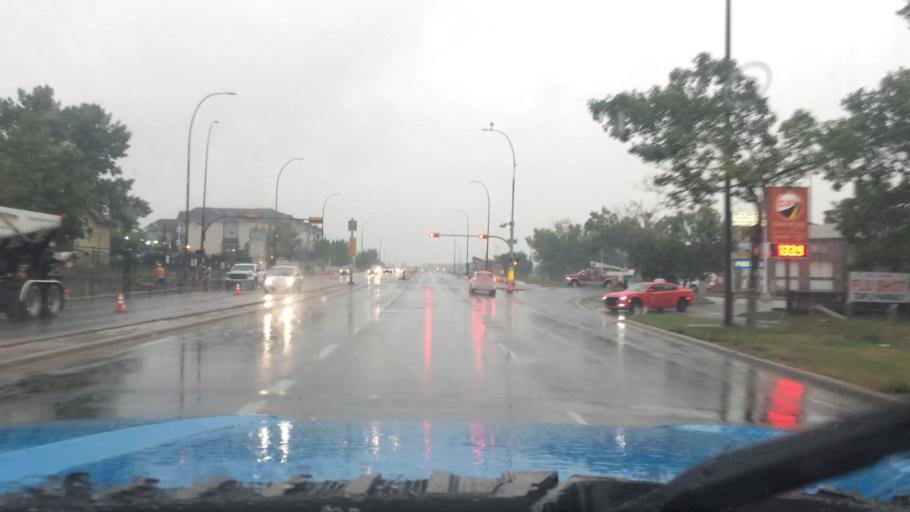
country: CA
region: Alberta
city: Calgary
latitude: 51.0906
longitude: -113.9585
